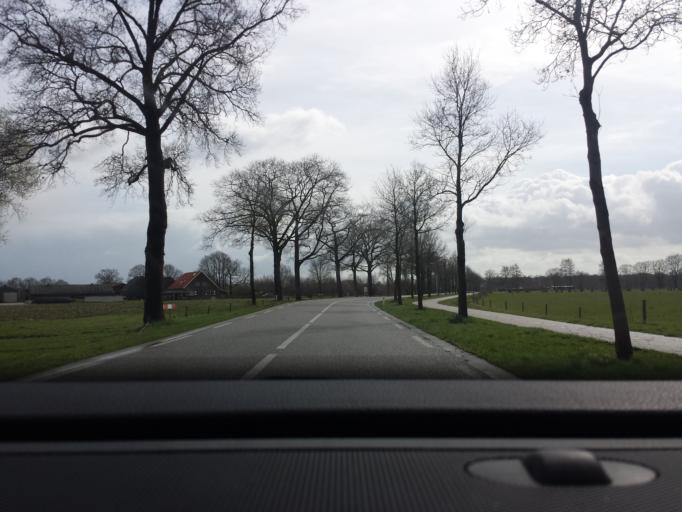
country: NL
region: Gelderland
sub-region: Oude IJsselstreek
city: Varsseveld
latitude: 51.9761
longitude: 6.4413
